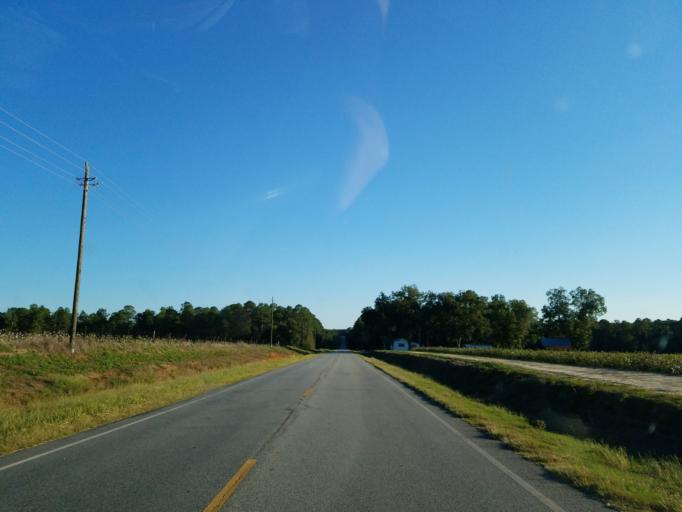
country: US
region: Georgia
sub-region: Worth County
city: Sylvester
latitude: 31.6077
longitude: -83.8645
